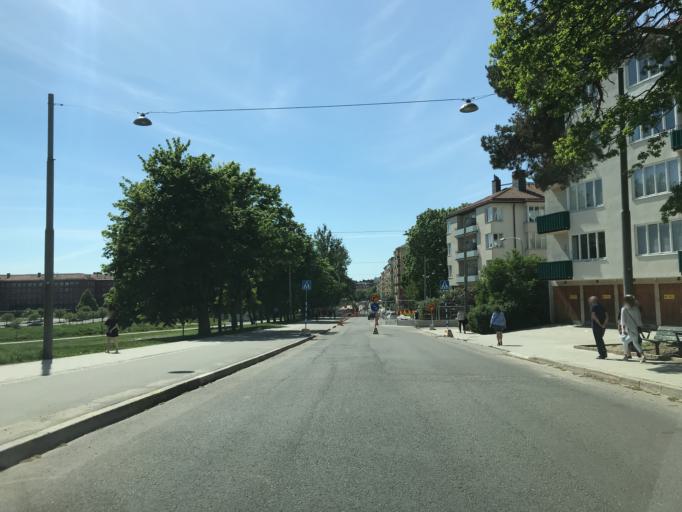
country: SE
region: Stockholm
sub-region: Stockholms Kommun
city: OEstermalm
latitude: 59.3448
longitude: 18.1013
